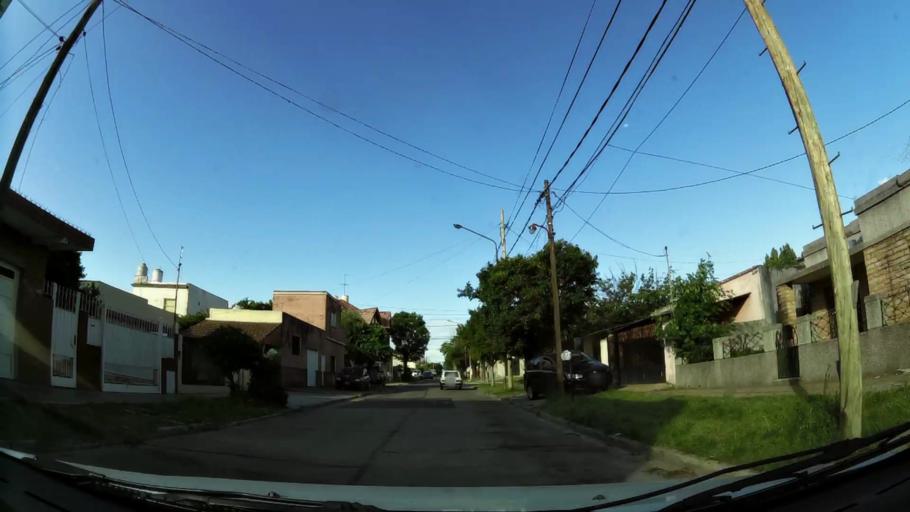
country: AR
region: Buenos Aires
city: Caseros
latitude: -34.5858
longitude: -58.5857
